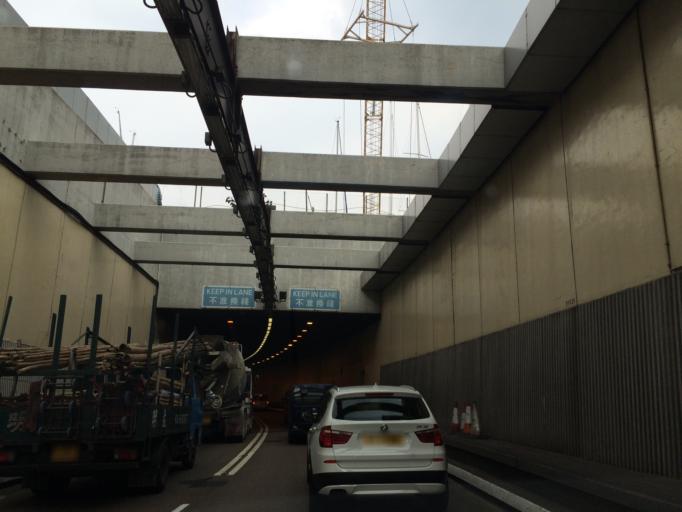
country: HK
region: Wanchai
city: Wan Chai
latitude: 22.2834
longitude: 114.1827
